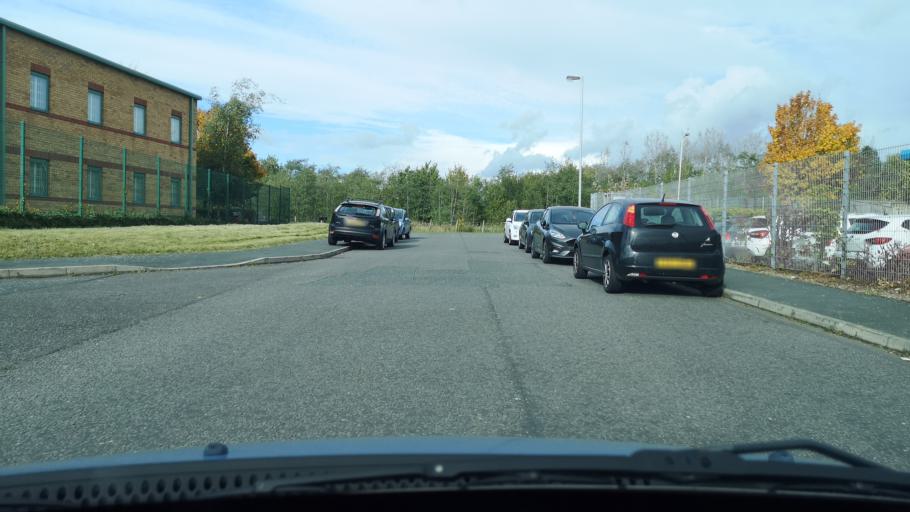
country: GB
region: England
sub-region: City and Borough of Wakefield
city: Featherstone
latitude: 53.6800
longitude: -1.3693
